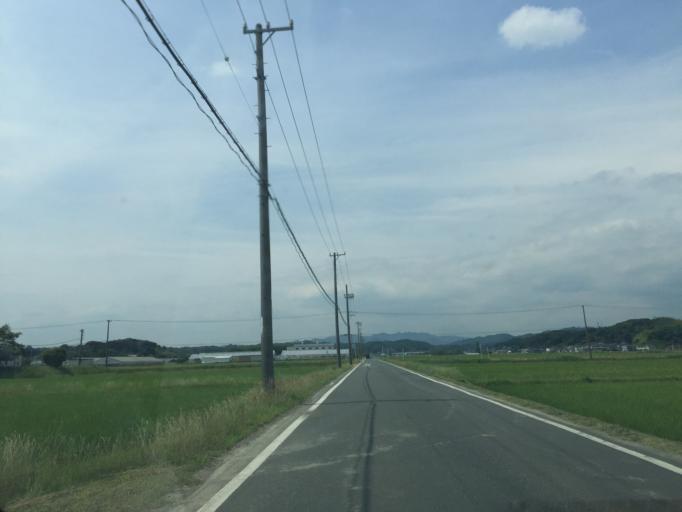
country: JP
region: Shizuoka
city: Mori
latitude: 34.7900
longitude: 137.9601
